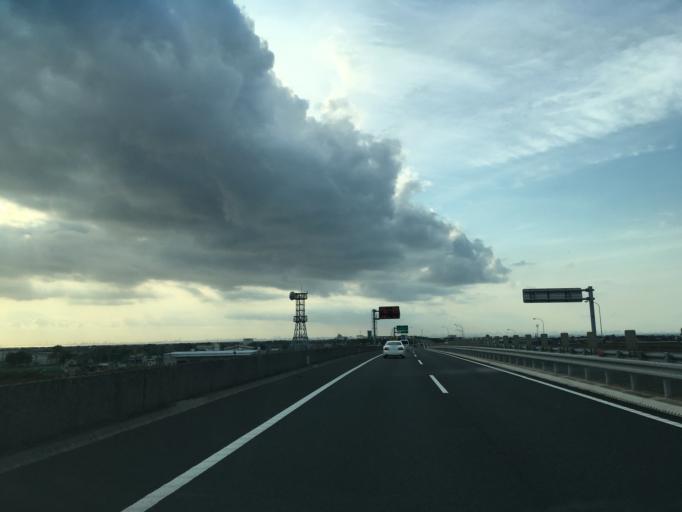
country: JP
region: Chiba
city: Kisarazu
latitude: 35.4249
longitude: 139.9320
